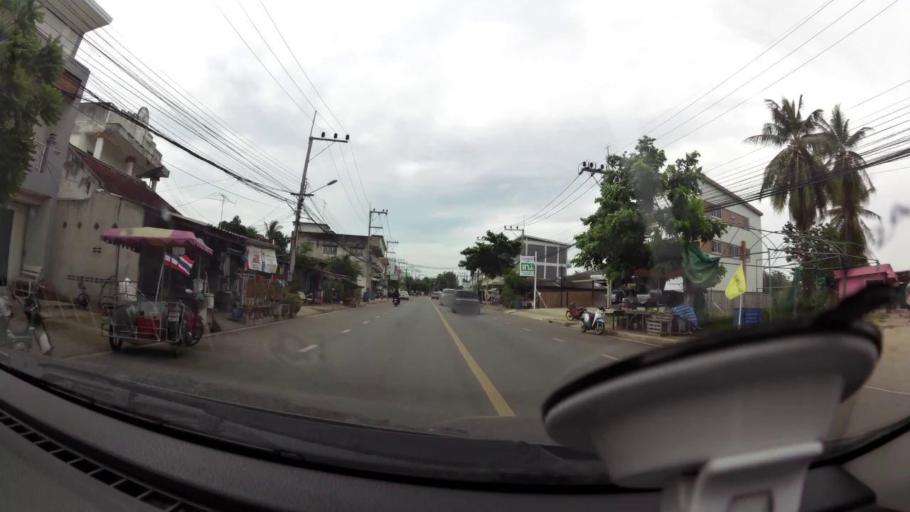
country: TH
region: Prachuap Khiri Khan
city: Pran Buri
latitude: 12.3920
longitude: 99.9871
